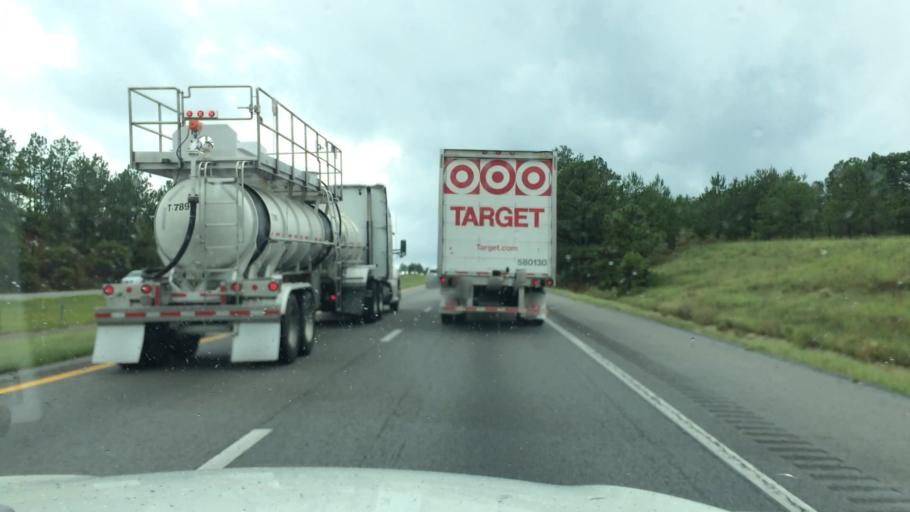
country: US
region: South Carolina
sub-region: Kershaw County
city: Lugoff
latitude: 34.1747
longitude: -80.7070
